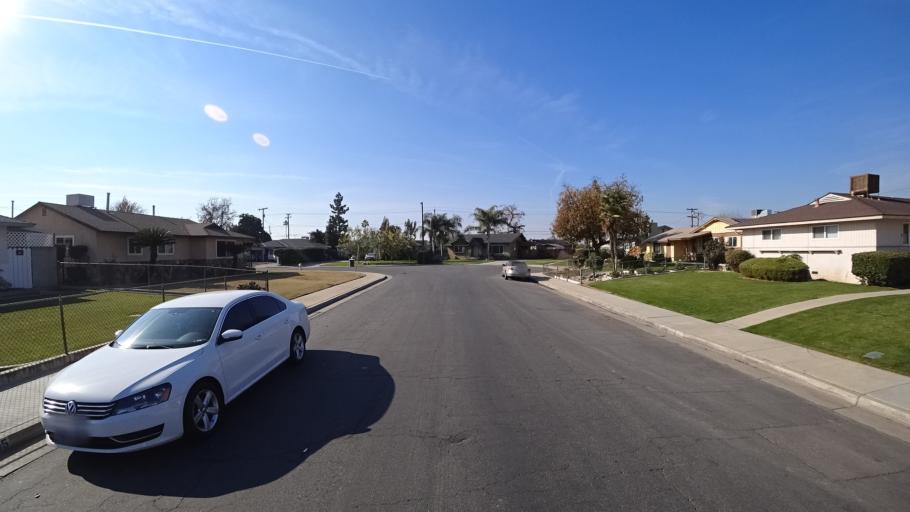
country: US
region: California
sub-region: Kern County
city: Bakersfield
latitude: 35.3312
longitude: -119.0198
